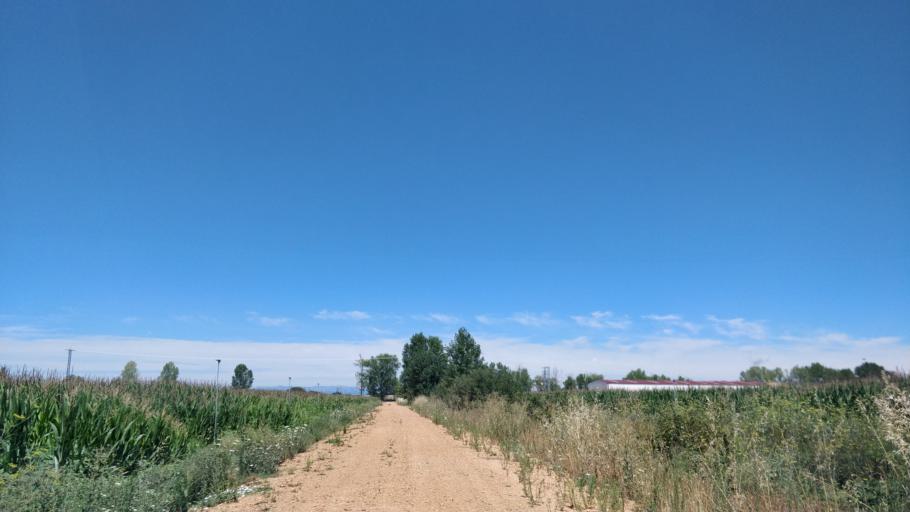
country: ES
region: Castille and Leon
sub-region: Provincia de Leon
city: Bustillo del Paramo
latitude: 42.4765
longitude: -5.8104
